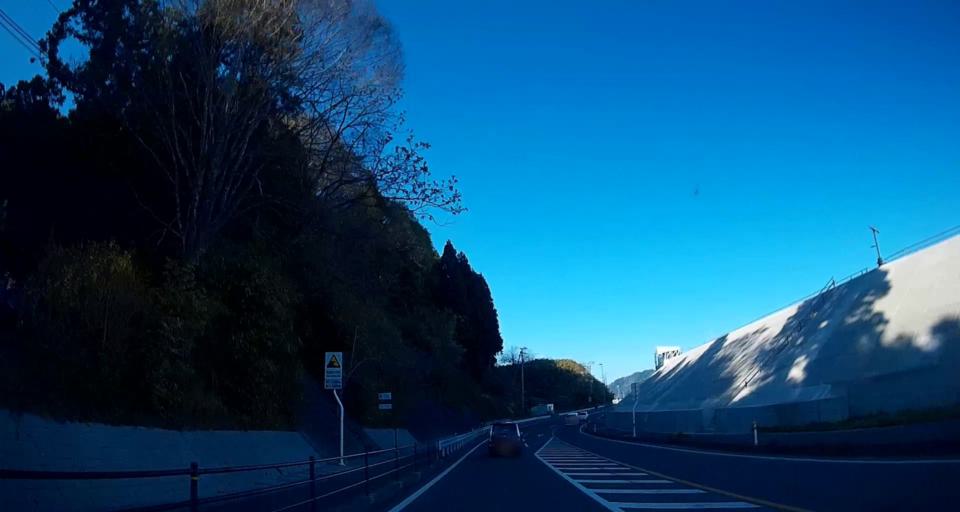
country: JP
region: Iwate
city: Miyako
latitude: 39.6014
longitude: 141.9471
